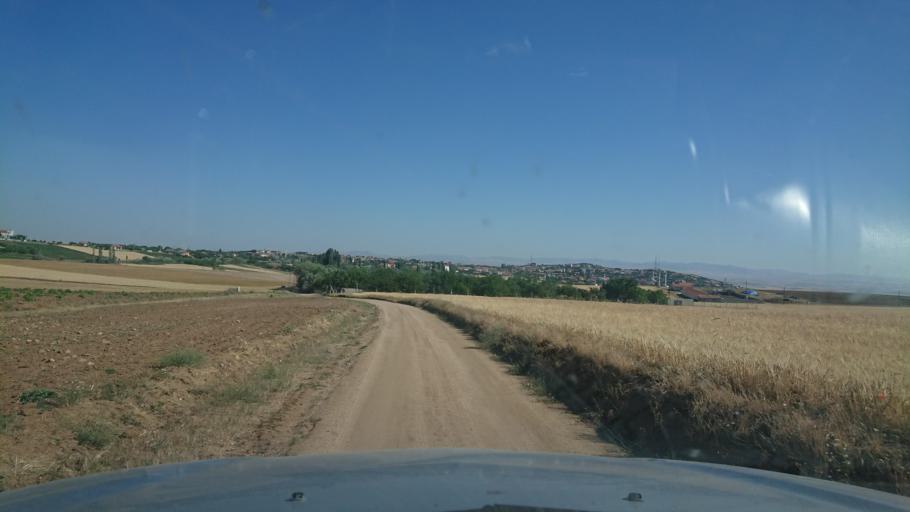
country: TR
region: Aksaray
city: Agacoren
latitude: 38.8557
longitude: 33.9137
